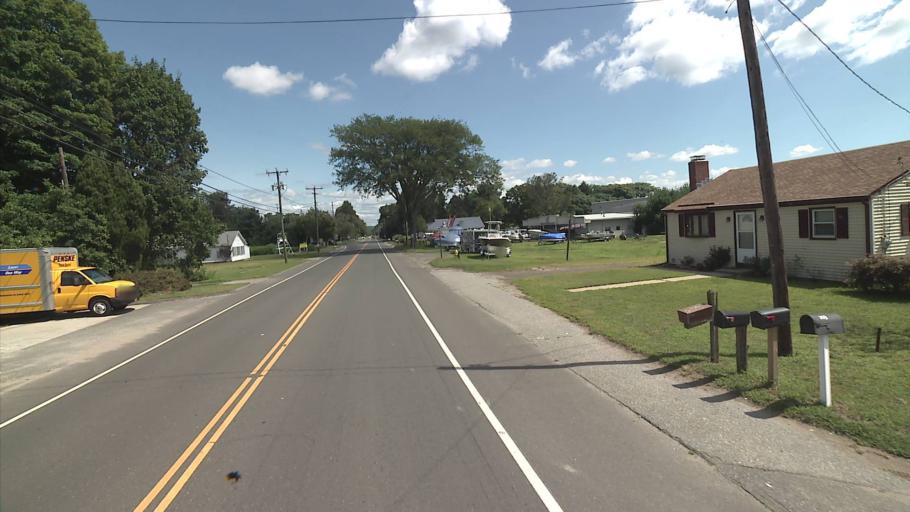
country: US
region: Connecticut
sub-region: Middlesex County
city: Old Saybrook Center
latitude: 41.3080
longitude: -72.3686
